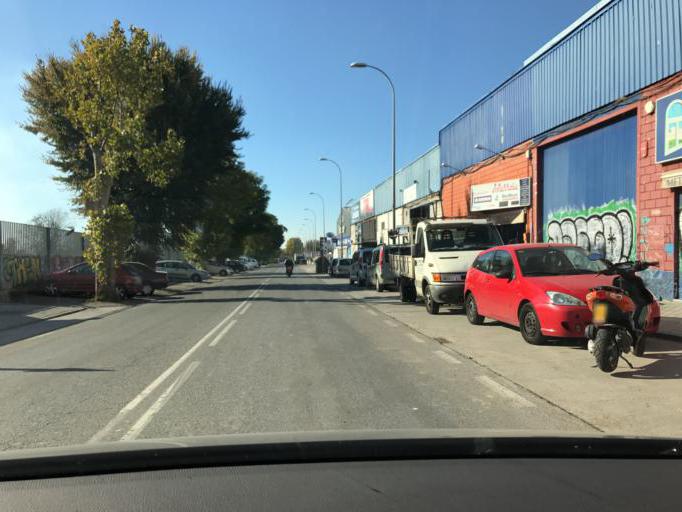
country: ES
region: Andalusia
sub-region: Provincia de Granada
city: Maracena
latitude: 37.1903
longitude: -3.6346
